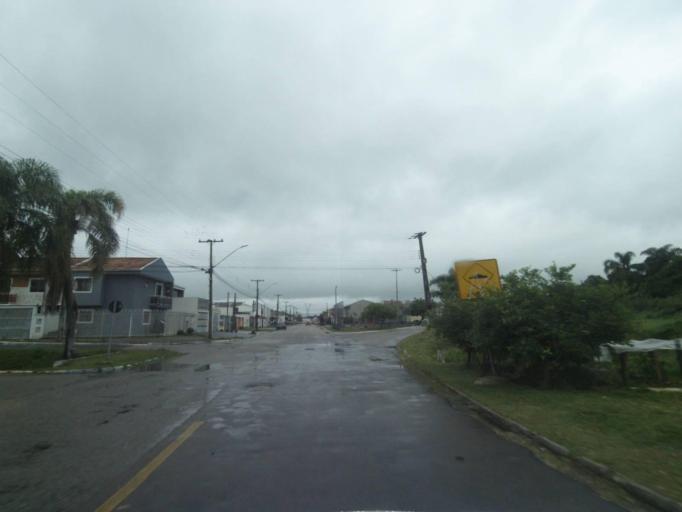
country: BR
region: Parana
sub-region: Araucaria
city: Araucaria
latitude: -25.5397
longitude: -49.3419
